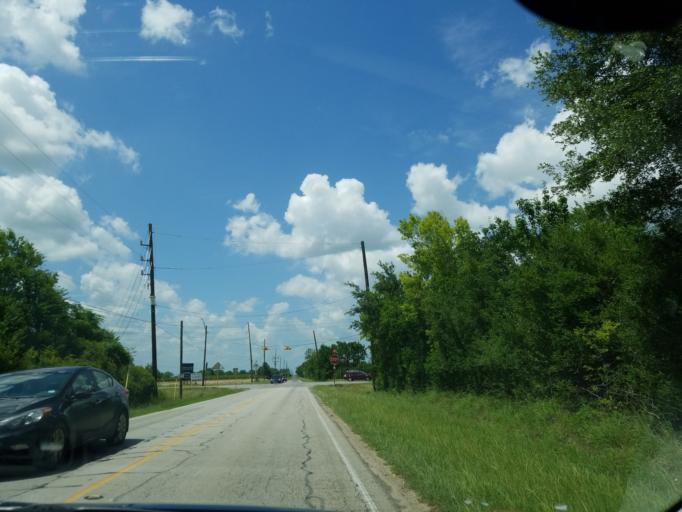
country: US
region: Texas
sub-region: Harris County
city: Katy
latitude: 29.8741
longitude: -95.8072
